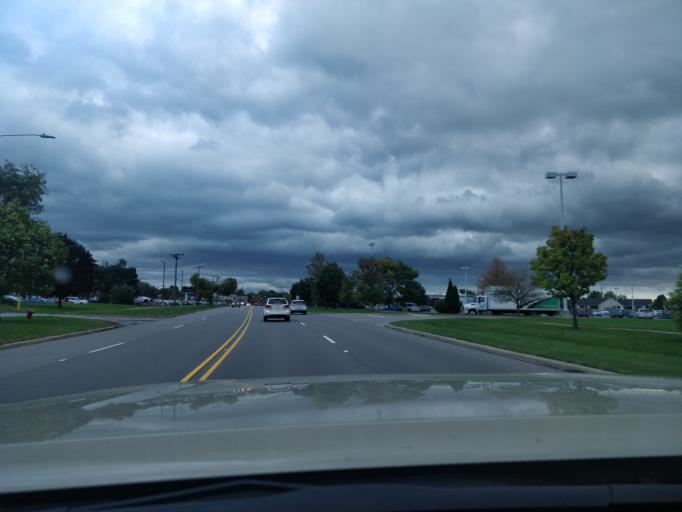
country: US
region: Michigan
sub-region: Wayne County
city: Riverview
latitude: 42.1879
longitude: -83.1923
